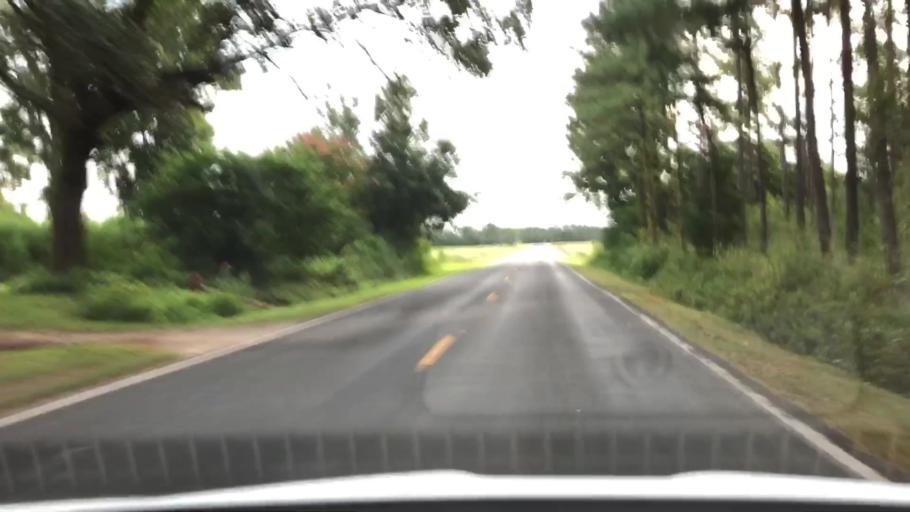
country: US
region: North Carolina
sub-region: Jones County
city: Trenton
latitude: 34.9982
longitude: -77.2774
